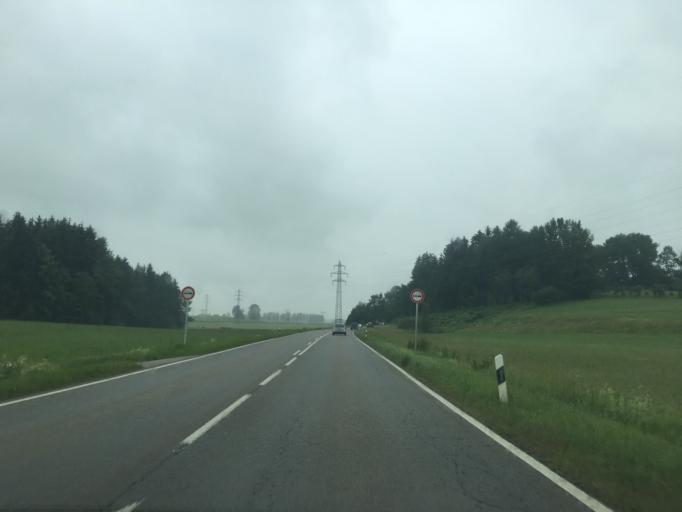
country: DE
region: Bavaria
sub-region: Upper Bavaria
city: Warngau
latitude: 47.8486
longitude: 11.7180
